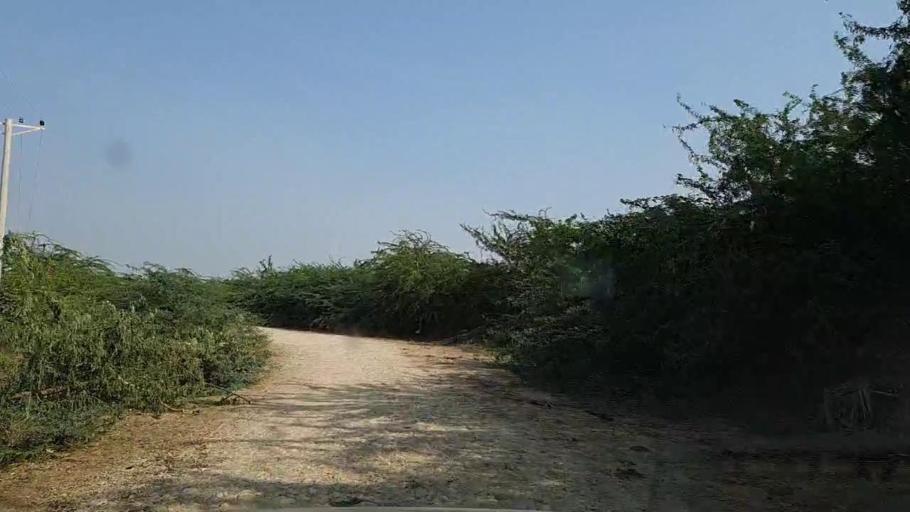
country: PK
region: Sindh
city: Mirpur Sakro
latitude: 24.5534
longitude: 67.5704
